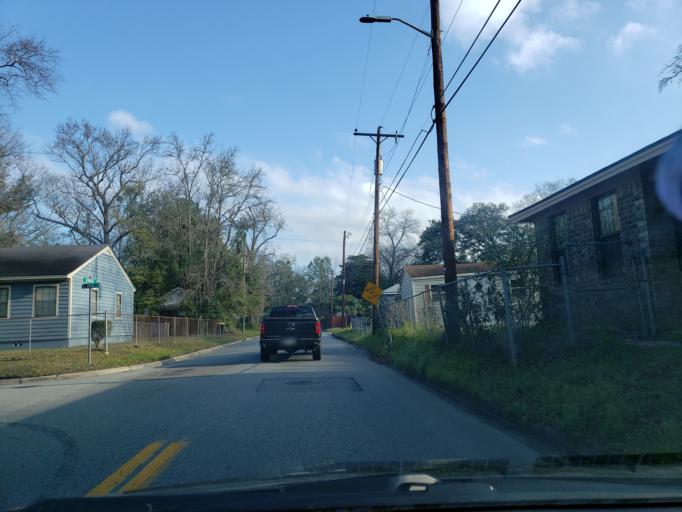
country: US
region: Georgia
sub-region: Chatham County
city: Thunderbolt
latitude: 32.0259
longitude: -81.0902
